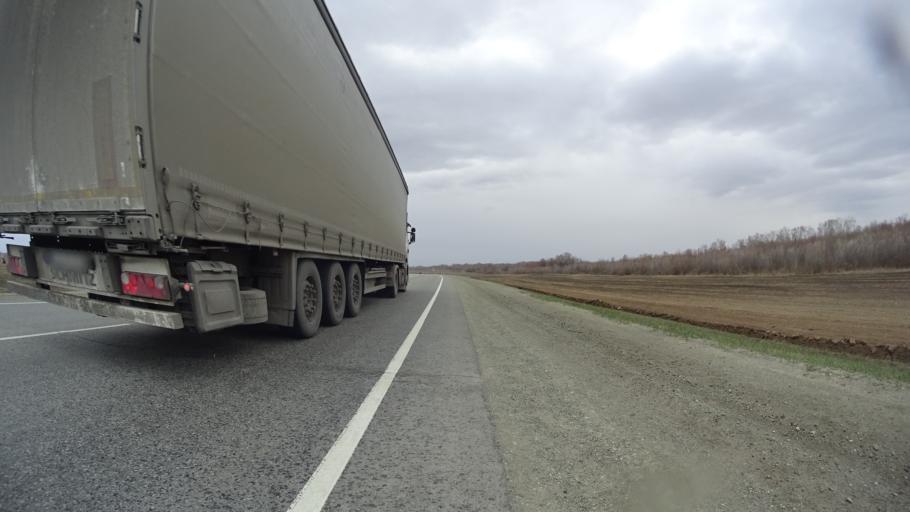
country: RU
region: Chelyabinsk
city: Krasnogorskiy
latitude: 54.6807
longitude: 61.2469
